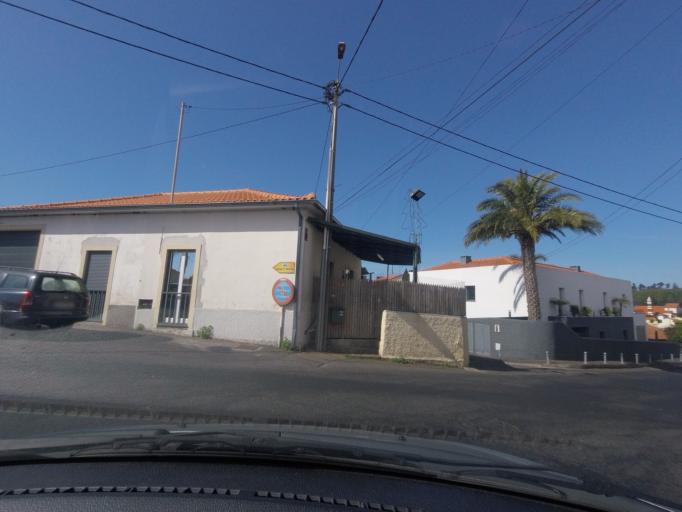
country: PT
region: Madeira
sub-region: Santa Cruz
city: Camacha
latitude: 32.6575
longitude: -16.8539
